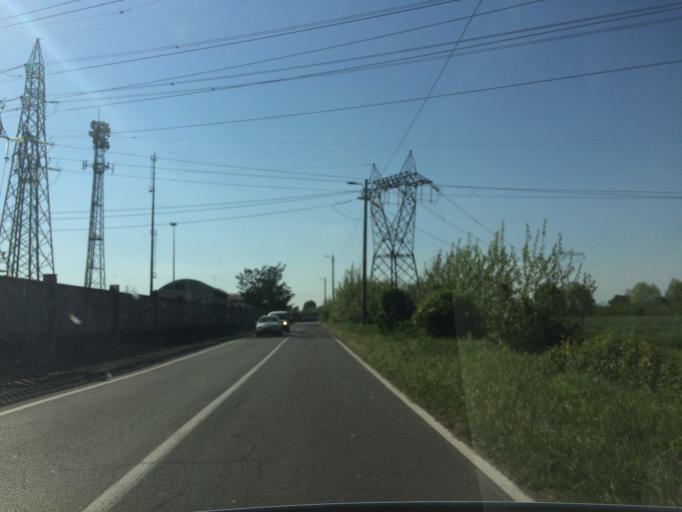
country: IT
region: Lombardy
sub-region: Provincia di Brescia
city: Folzano
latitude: 45.4920
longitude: 10.1958
